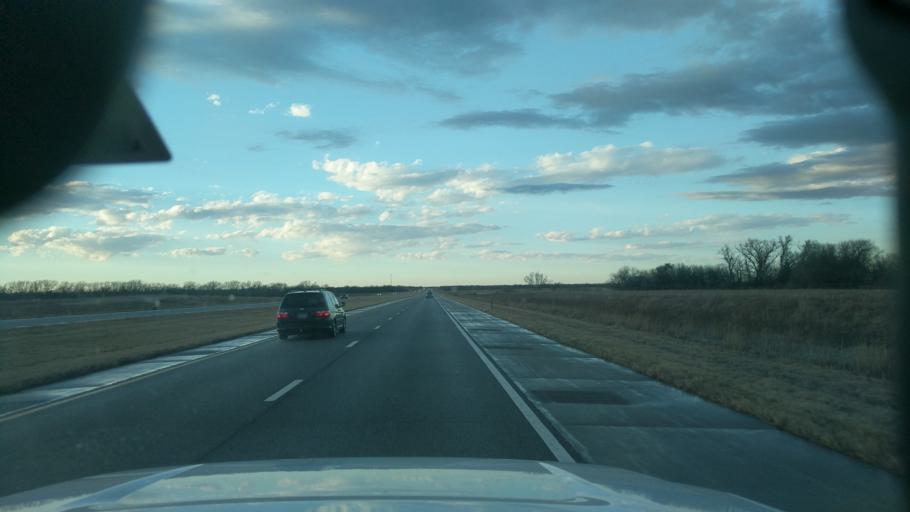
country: US
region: Kansas
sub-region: Harvey County
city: Hesston
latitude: 38.1746
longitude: -97.4475
